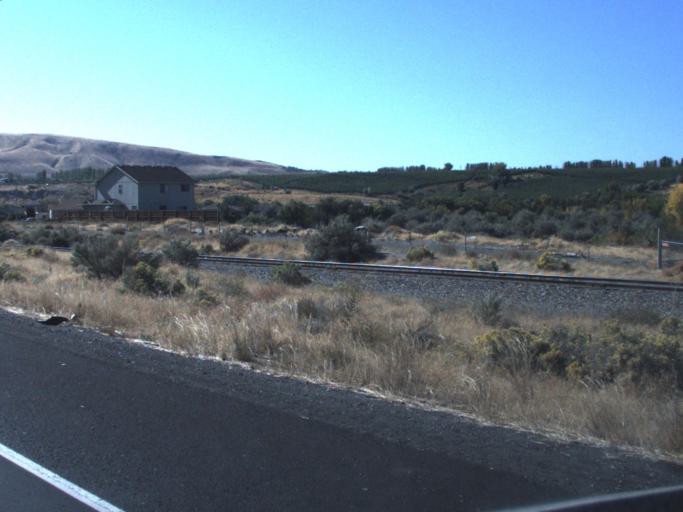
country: US
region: Washington
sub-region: Benton County
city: Richland
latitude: 46.2769
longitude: -119.3067
